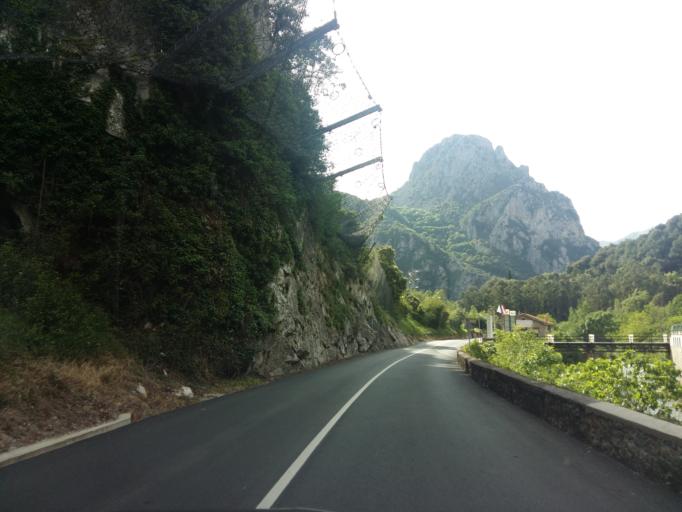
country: ES
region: Cantabria
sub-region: Provincia de Cantabria
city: Tresviso
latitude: 43.2514
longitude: -4.6061
